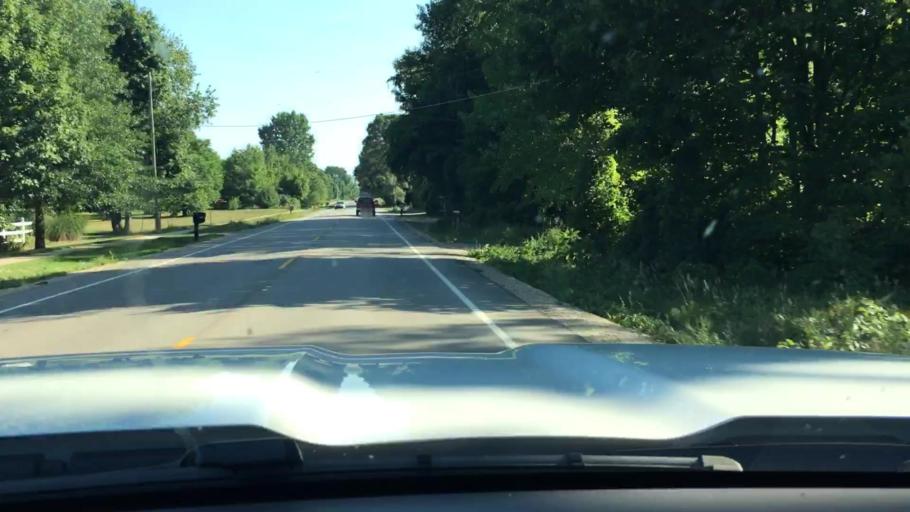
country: US
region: Michigan
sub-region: Ottawa County
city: Allendale
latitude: 42.9550
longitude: -85.9534
